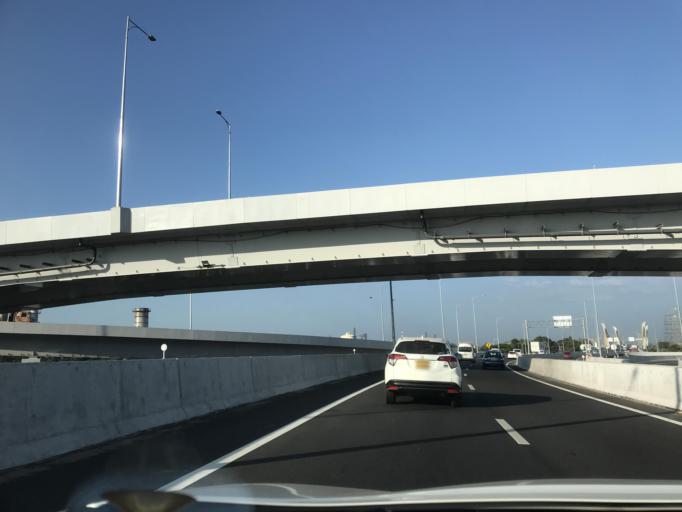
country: LK
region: Western
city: Kolonnawa
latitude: 6.9497
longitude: 79.8786
